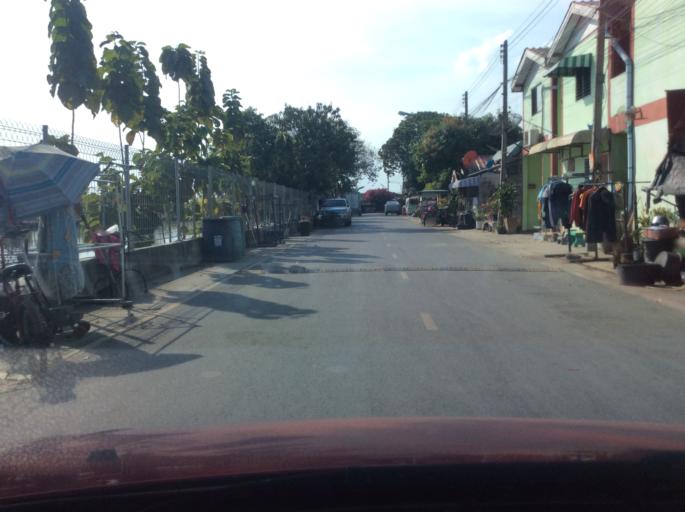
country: TH
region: Pathum Thani
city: Lam Luk Ka
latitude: 13.9674
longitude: 100.7397
